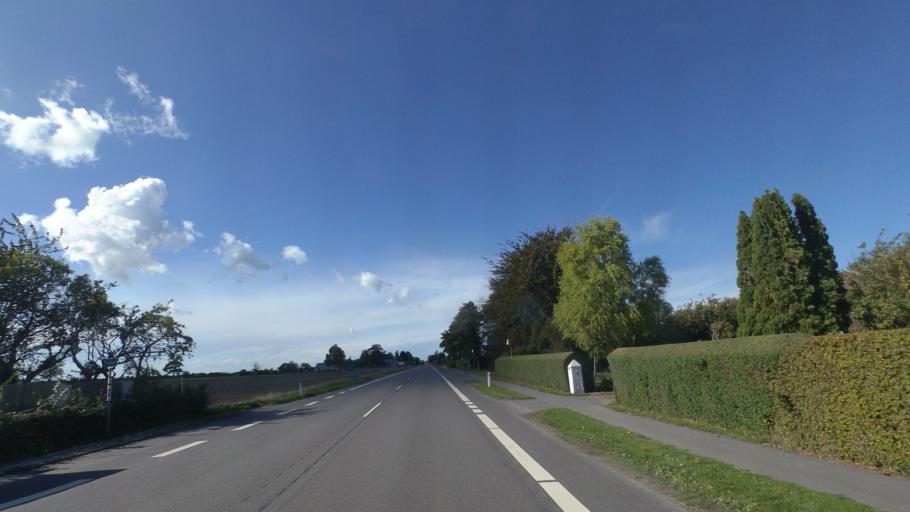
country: DK
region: Capital Region
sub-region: Bornholm Kommune
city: Ronne
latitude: 55.0713
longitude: 14.8097
